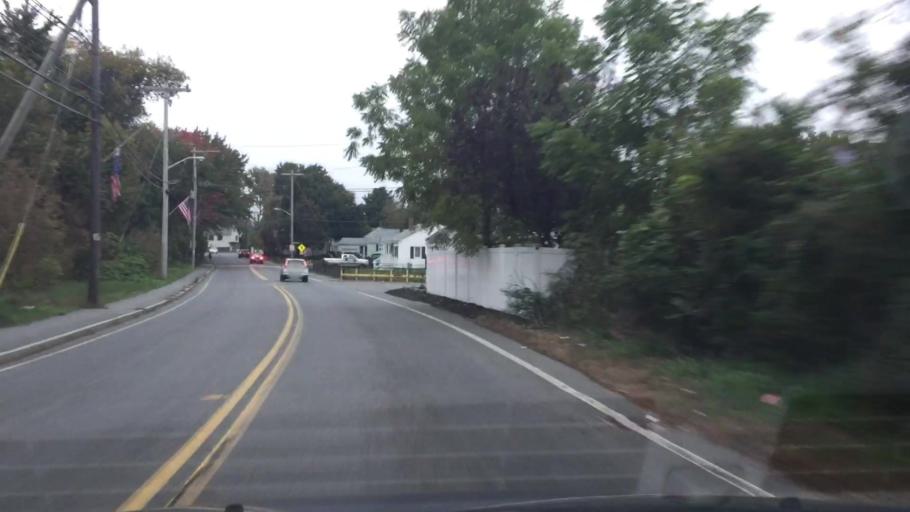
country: US
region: Massachusetts
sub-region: Middlesex County
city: Dracut
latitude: 42.6681
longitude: -71.3075
